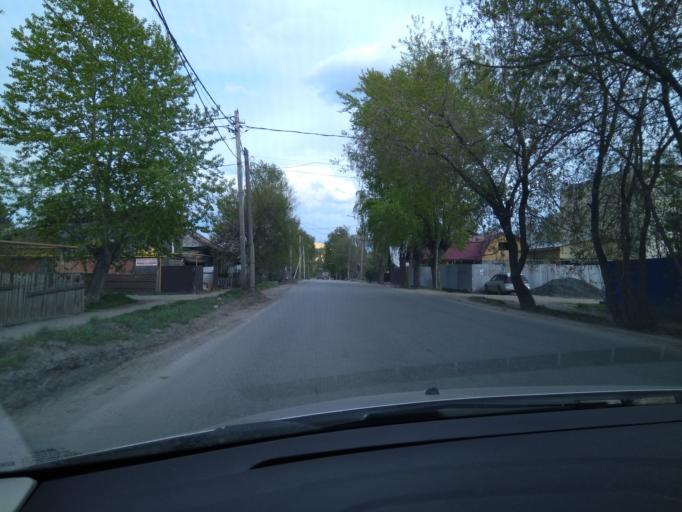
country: RU
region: Sverdlovsk
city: Yekaterinburg
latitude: 56.8814
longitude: 60.5543
